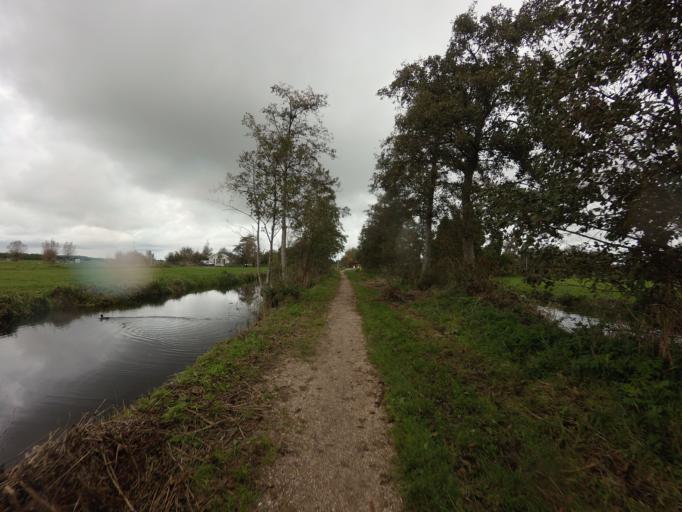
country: NL
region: South Holland
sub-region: Gemeente Alphen aan den Rijn
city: Alphen aan den Rijn
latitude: 52.1060
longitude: 4.6494
